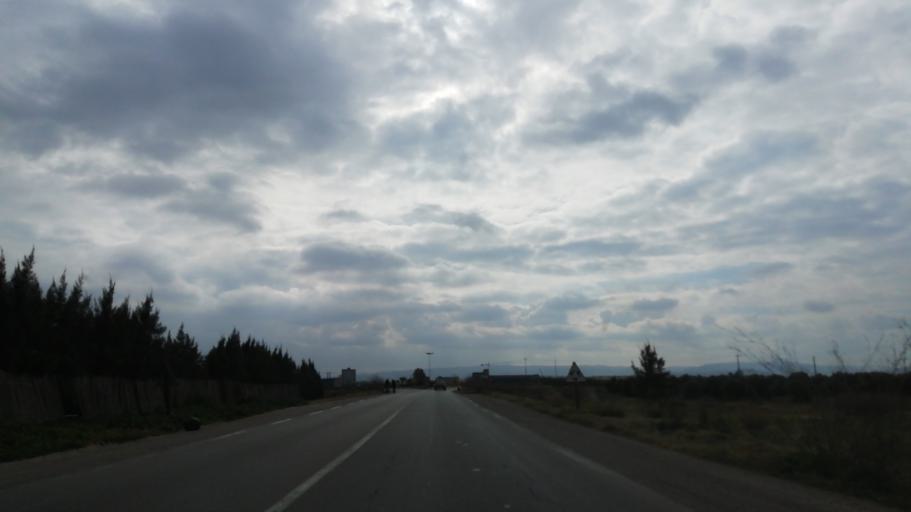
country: DZ
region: Oran
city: Sidi ech Chahmi
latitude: 35.5688
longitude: -0.4502
